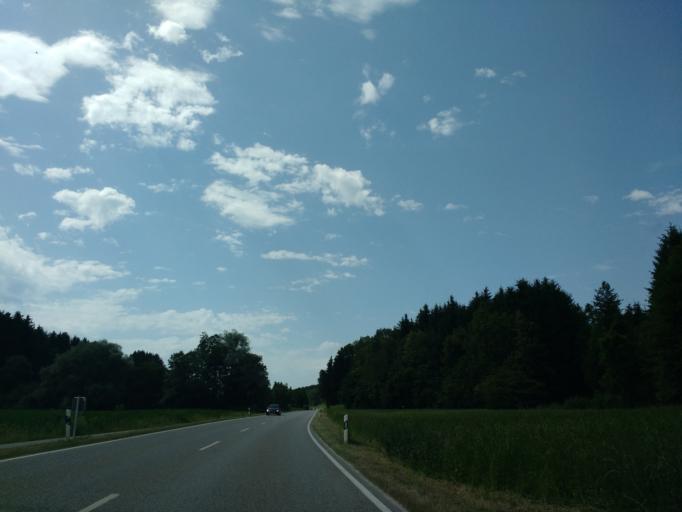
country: DE
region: Bavaria
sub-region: Upper Bavaria
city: Seeon-Seebruck
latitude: 47.9973
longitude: 12.4498
